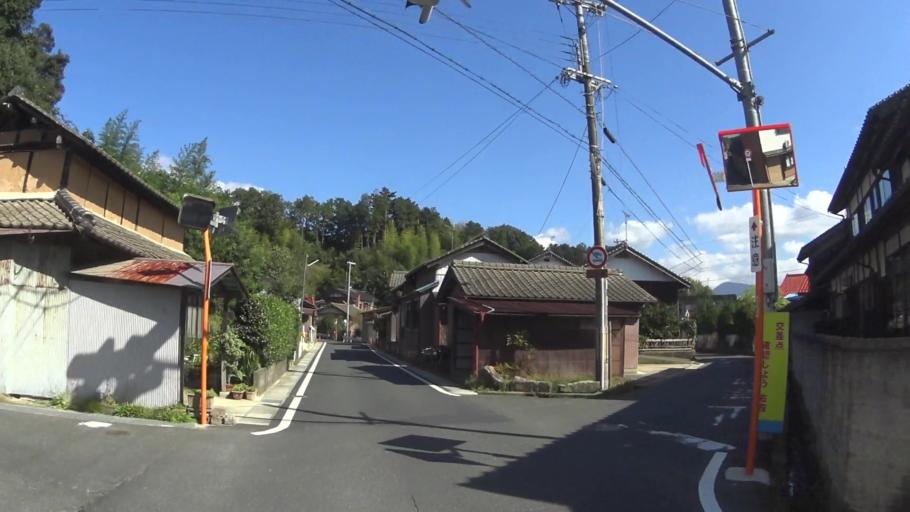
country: JP
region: Kyoto
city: Miyazu
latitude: 35.6323
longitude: 135.0722
